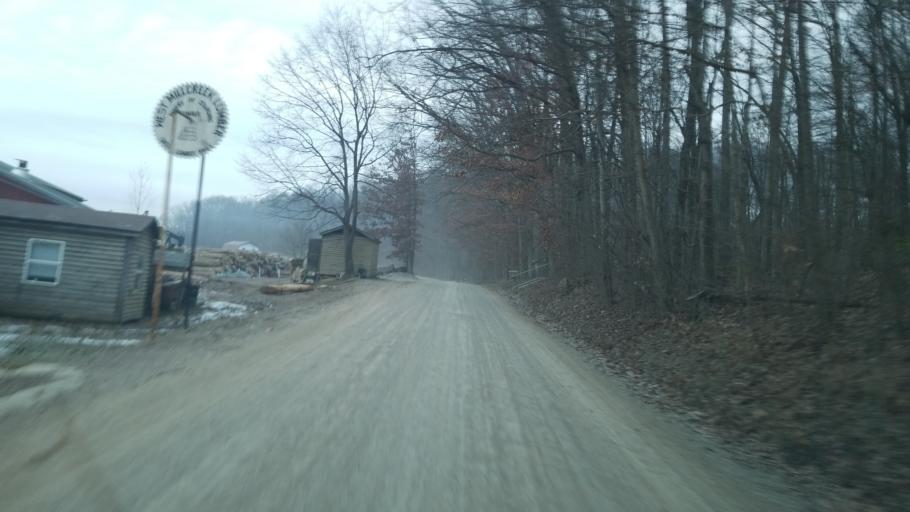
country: US
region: Ohio
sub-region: Holmes County
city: Millersburg
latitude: 40.4565
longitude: -81.8613
